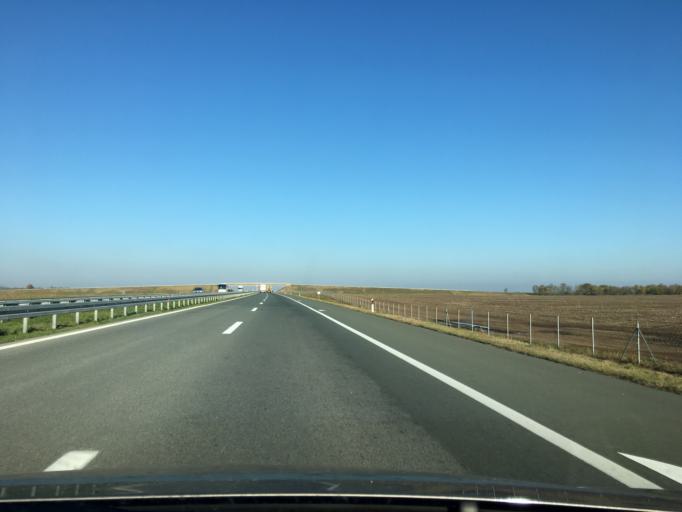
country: RS
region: Autonomna Pokrajina Vojvodina
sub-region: Severnobacki Okrug
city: Mali Igos
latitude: 45.6927
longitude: 19.7247
